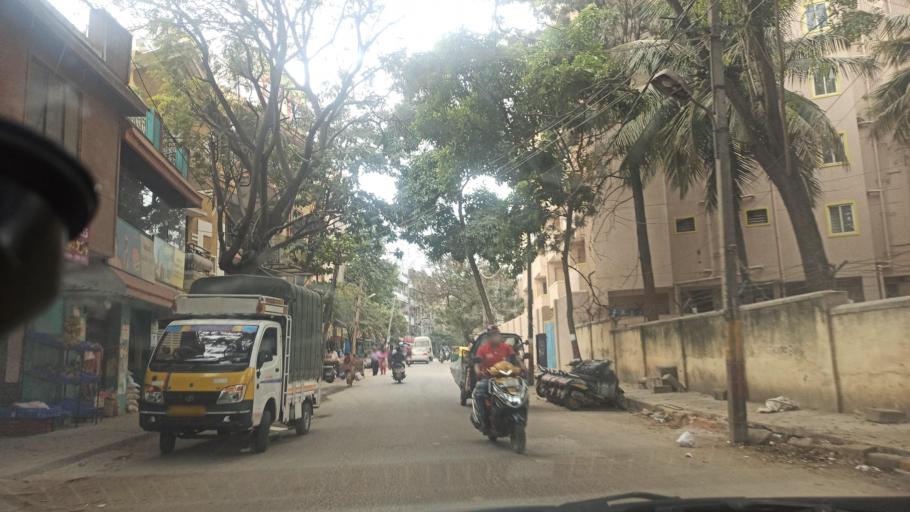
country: IN
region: Karnataka
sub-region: Bangalore Urban
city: Yelahanka
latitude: 13.0394
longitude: 77.6230
